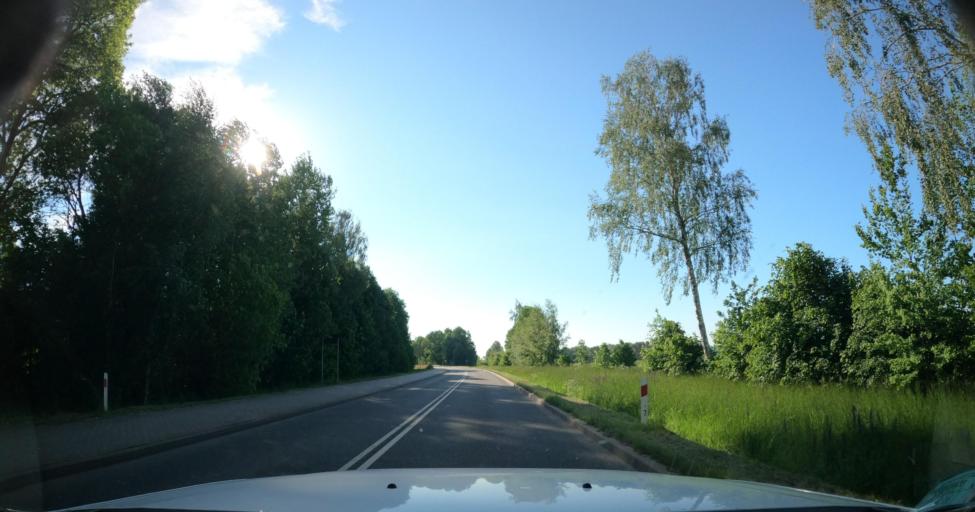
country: PL
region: Warmian-Masurian Voivodeship
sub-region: Powiat elblaski
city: Paslek
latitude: 54.0814
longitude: 19.6206
